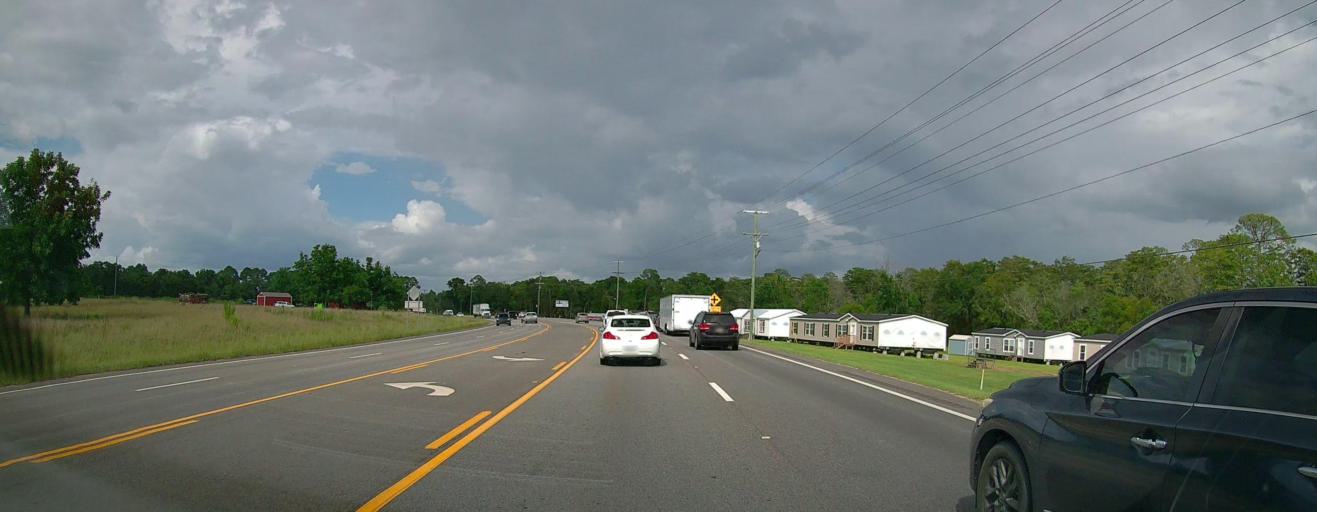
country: US
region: Georgia
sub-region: Coffee County
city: Douglas
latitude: 31.4904
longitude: -82.8341
